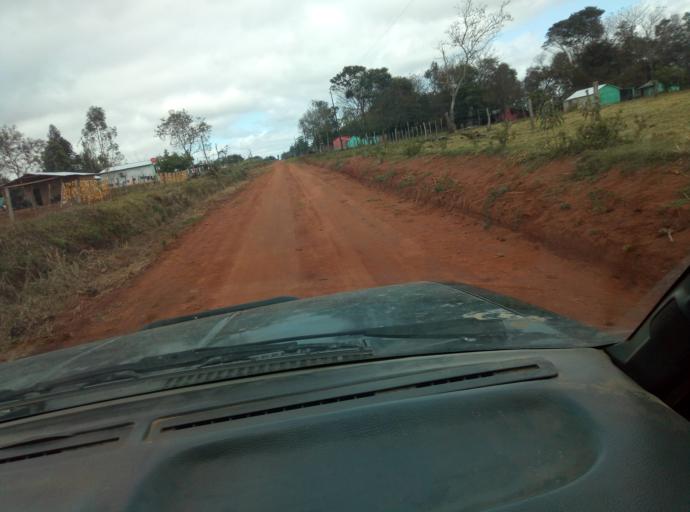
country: PY
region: Caaguazu
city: Doctor Cecilio Baez
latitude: -25.1479
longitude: -56.2905
